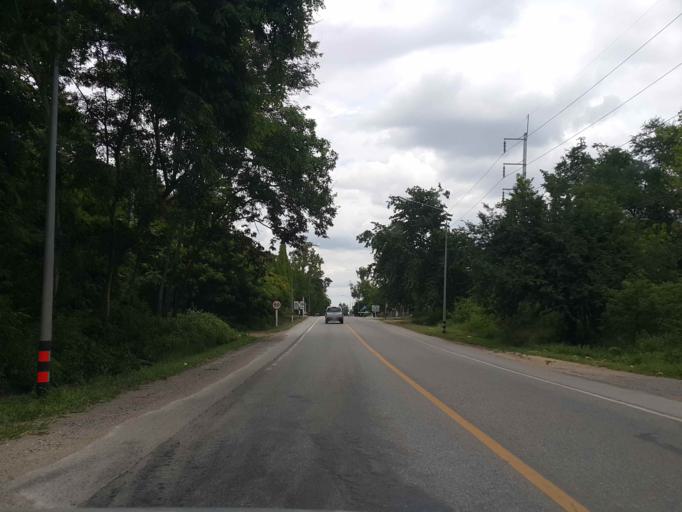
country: TH
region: Chiang Mai
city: Doi Lo
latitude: 18.4247
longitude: 98.8610
